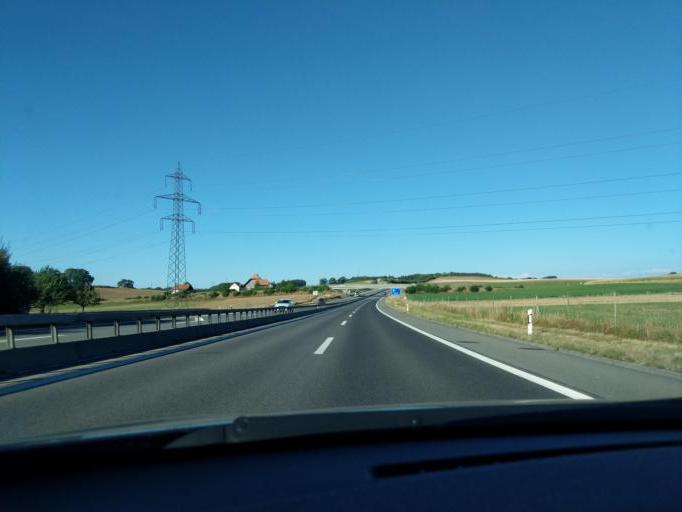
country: CH
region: Fribourg
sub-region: Sense District
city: Dudingen
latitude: 46.8659
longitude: 7.2116
